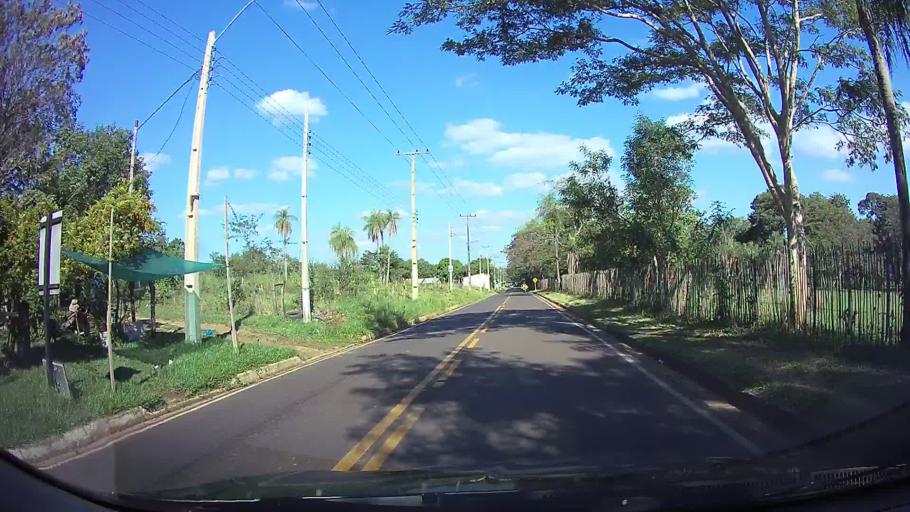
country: PY
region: Central
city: Limpio
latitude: -25.2093
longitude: -57.4791
